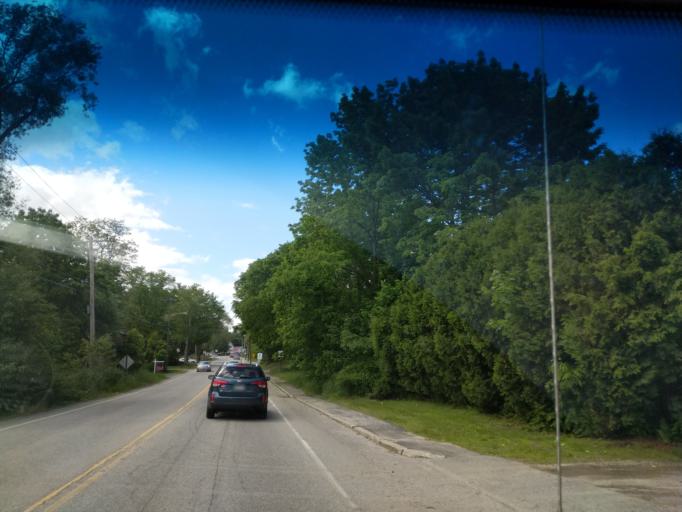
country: US
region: Maine
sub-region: Cumberland County
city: South Windham
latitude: 43.7267
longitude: -70.4230
